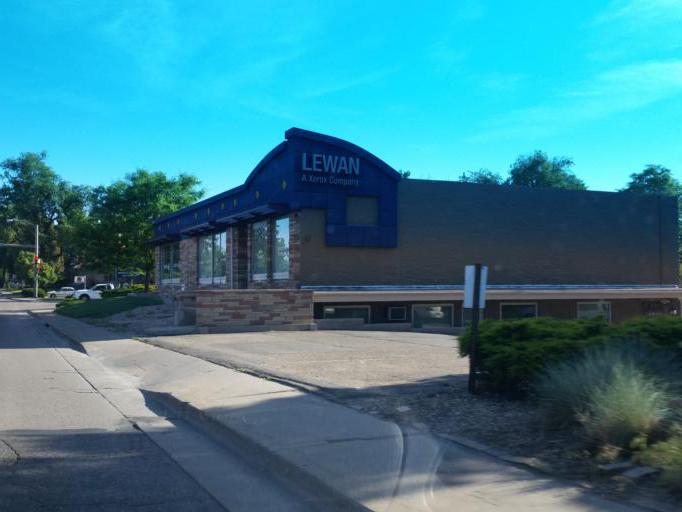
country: US
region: Colorado
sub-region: Larimer County
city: Fort Collins
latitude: 40.5663
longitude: -105.0769
